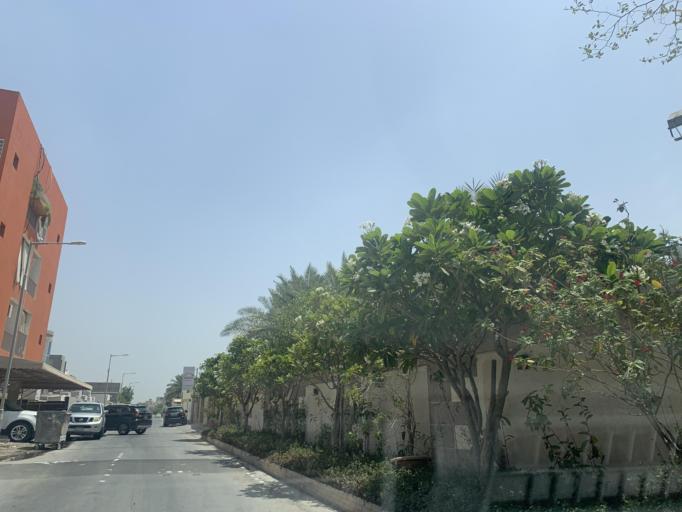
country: BH
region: Central Governorate
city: Madinat Hamad
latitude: 26.1489
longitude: 50.5047
